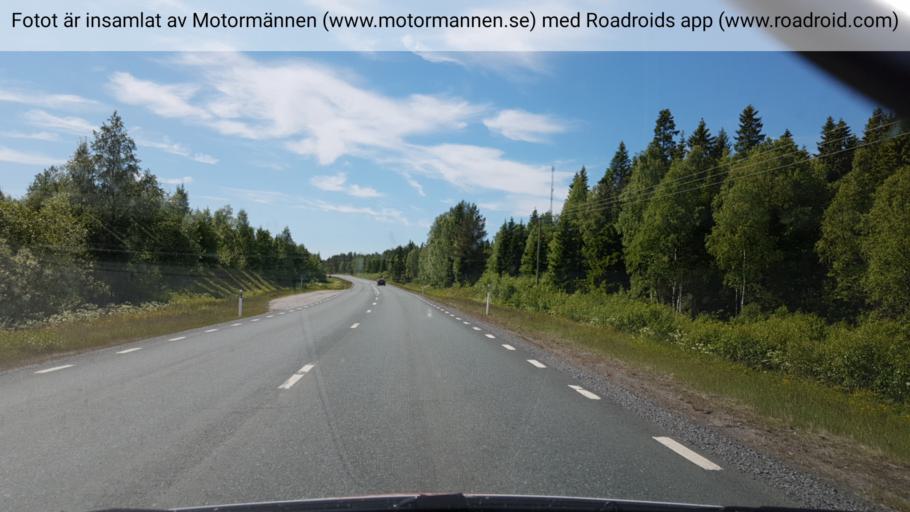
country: SE
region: Norrbotten
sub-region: Haparanda Kommun
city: Haparanda
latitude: 65.8204
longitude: 24.0343
